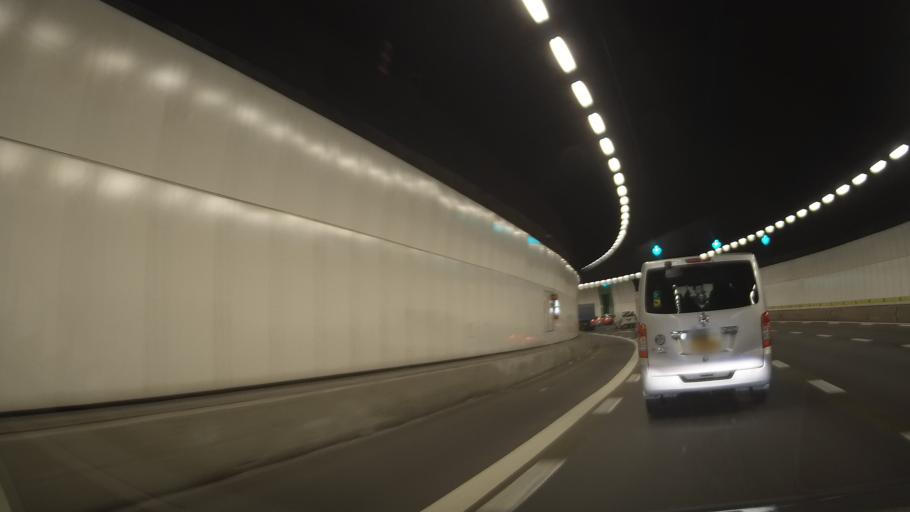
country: SG
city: Singapore
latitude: 1.3349
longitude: 103.8894
